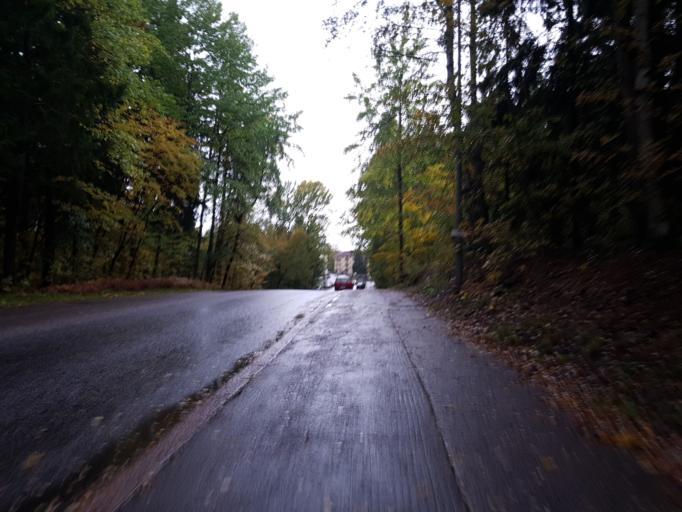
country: FI
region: Uusimaa
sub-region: Helsinki
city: Helsinki
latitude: 60.2238
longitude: 24.9330
